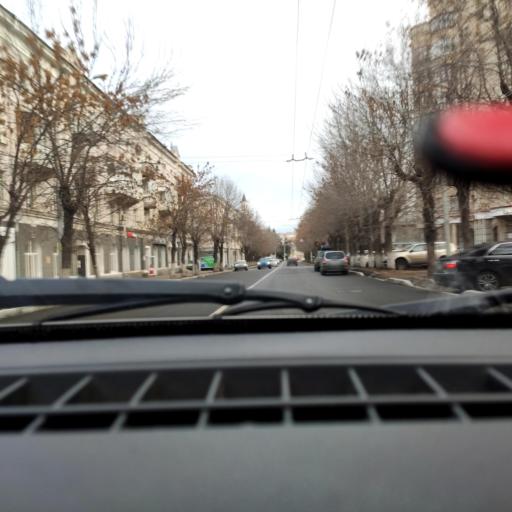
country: RU
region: Bashkortostan
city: Ufa
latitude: 54.7375
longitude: 55.9465
